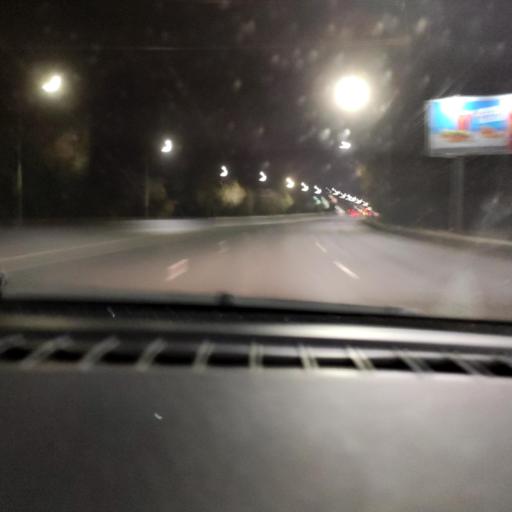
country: RU
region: Voronezj
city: Voronezh
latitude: 51.6373
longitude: 39.2083
